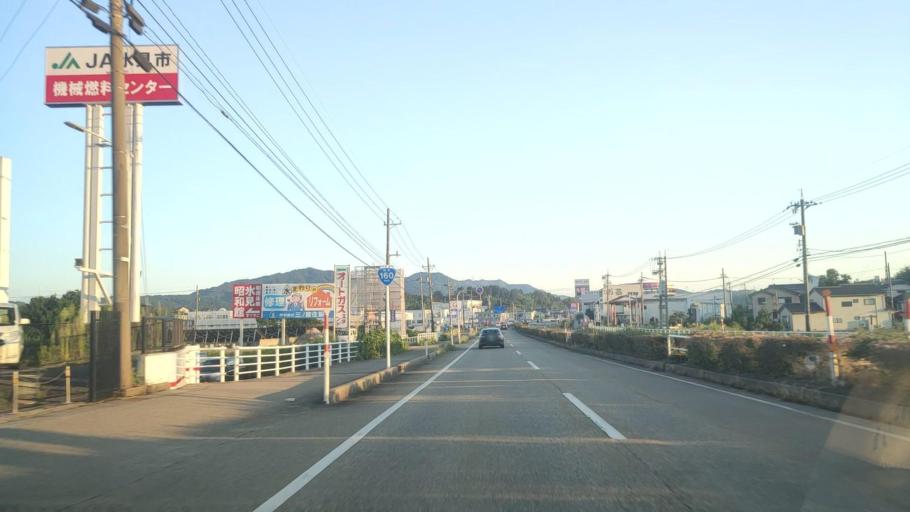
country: JP
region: Toyama
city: Himi
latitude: 36.8267
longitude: 136.9938
